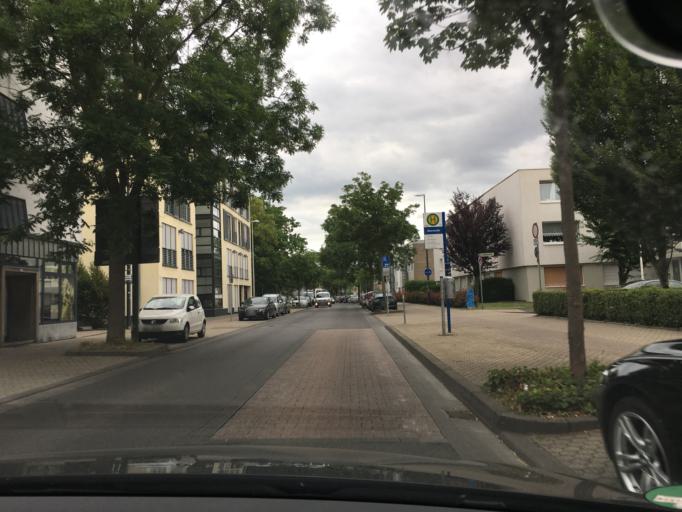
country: DE
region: North Rhine-Westphalia
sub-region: Regierungsbezirk Koln
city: Dueren
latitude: 50.7992
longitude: 6.4852
